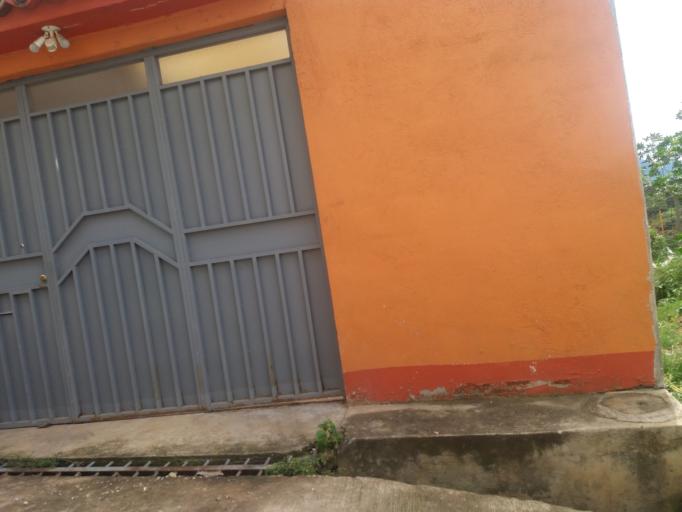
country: GT
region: Guatemala
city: Petapa
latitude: 14.5376
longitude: -90.5262
